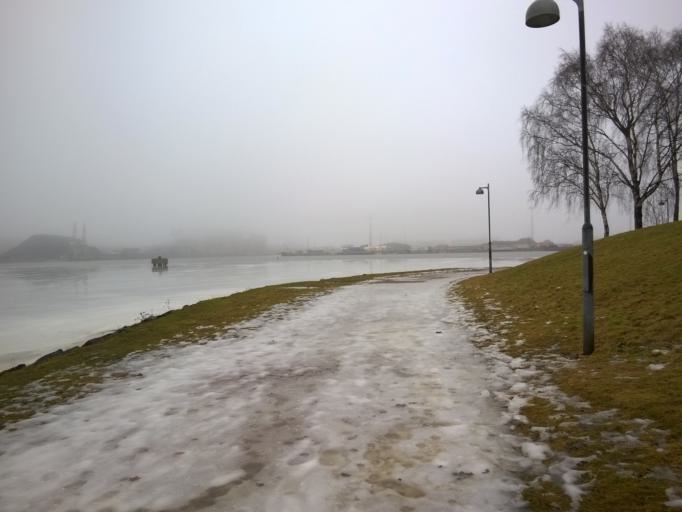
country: FI
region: Uusimaa
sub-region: Helsinki
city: Helsinki
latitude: 60.1742
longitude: 24.9674
